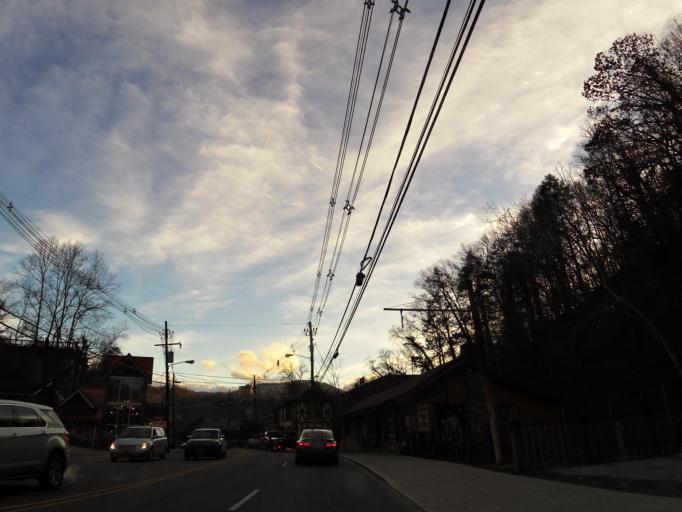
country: US
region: Tennessee
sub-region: Sevier County
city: Gatlinburg
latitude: 35.7175
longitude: -83.5113
